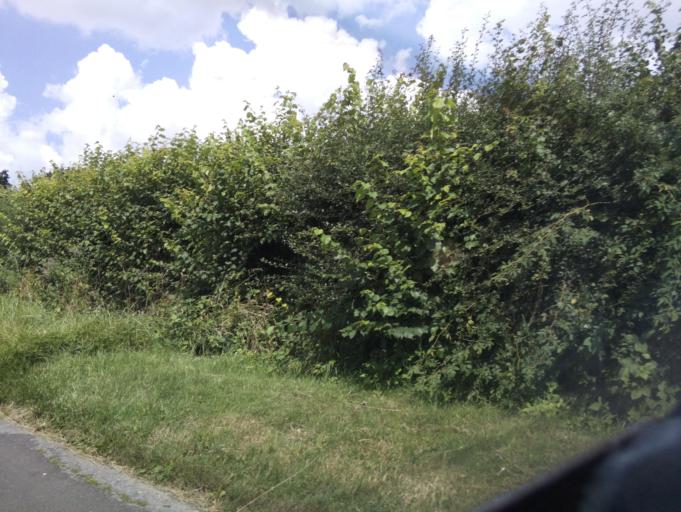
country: GB
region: England
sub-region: Wiltshire
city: Hankerton
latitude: 51.6326
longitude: -2.0522
